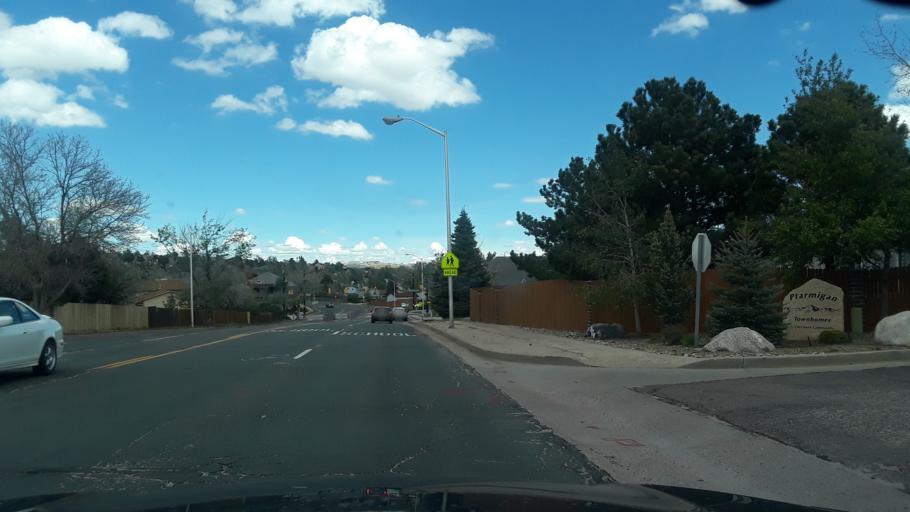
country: US
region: Colorado
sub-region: El Paso County
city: Black Forest
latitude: 38.9417
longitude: -104.7652
